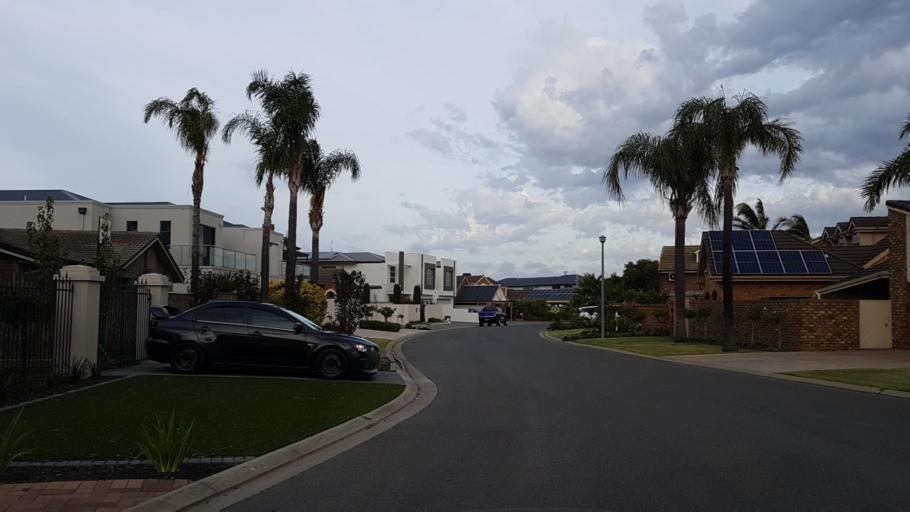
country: AU
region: South Australia
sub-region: Charles Sturt
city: West Lakes Shore
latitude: -34.8596
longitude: 138.4982
